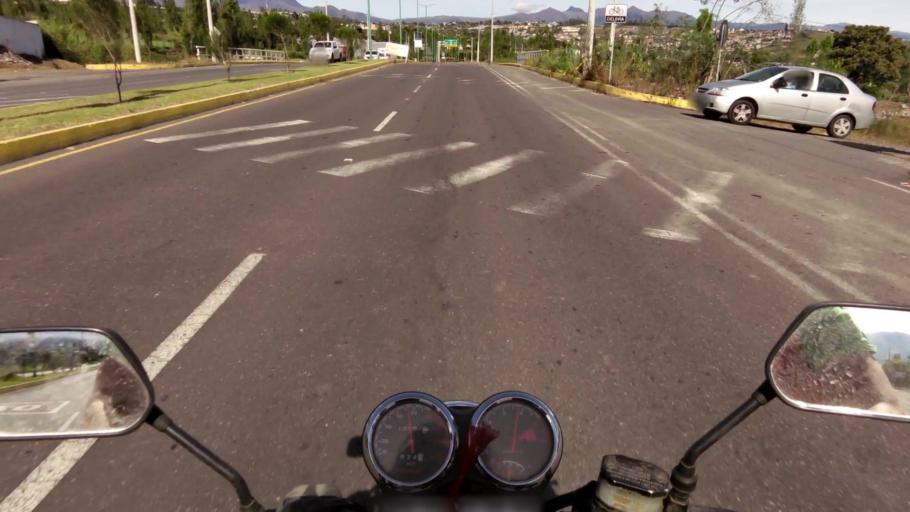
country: EC
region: Imbabura
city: Ibarra
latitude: 0.3326
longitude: -78.1546
